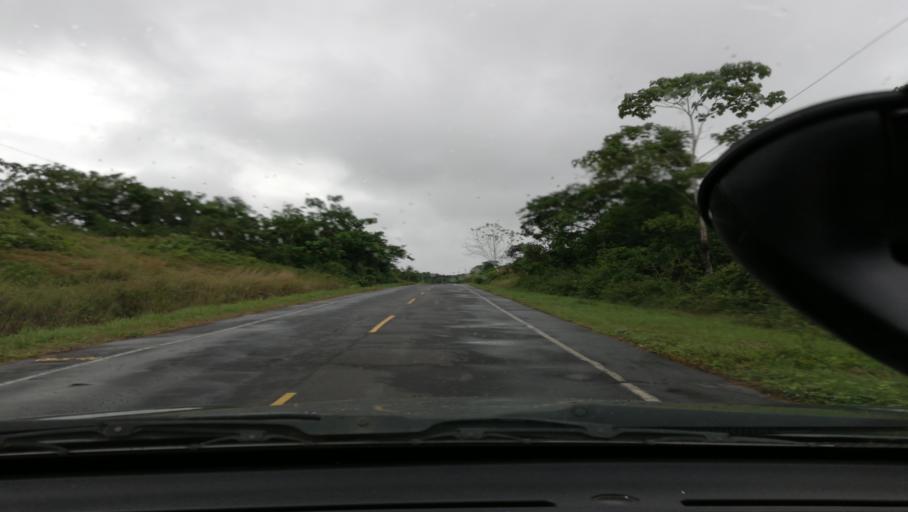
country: PE
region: Loreto
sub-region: Provincia de Loreto
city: Nauta
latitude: -4.3350
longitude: -73.5353
